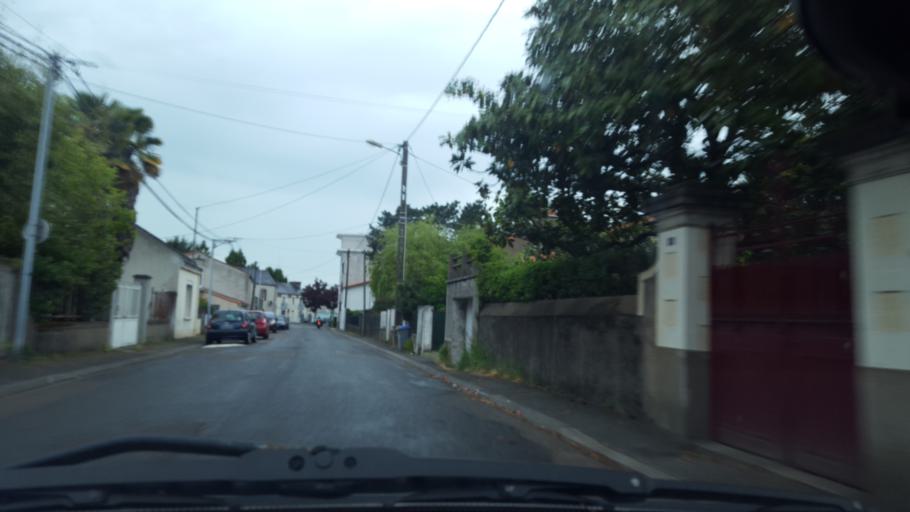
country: FR
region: Pays de la Loire
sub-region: Departement de la Loire-Atlantique
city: Reze
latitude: 47.1772
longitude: -1.5428
